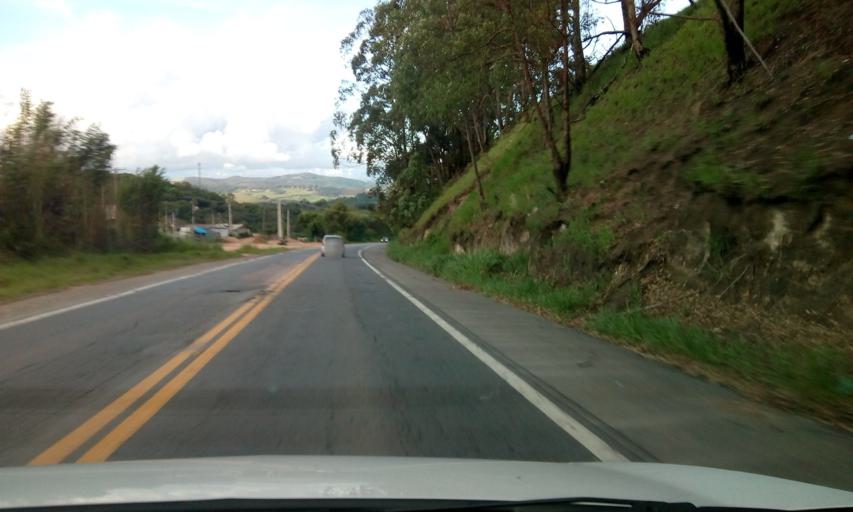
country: BR
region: Sao Paulo
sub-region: Itatiba
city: Itatiba
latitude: -23.0045
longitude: -46.8167
